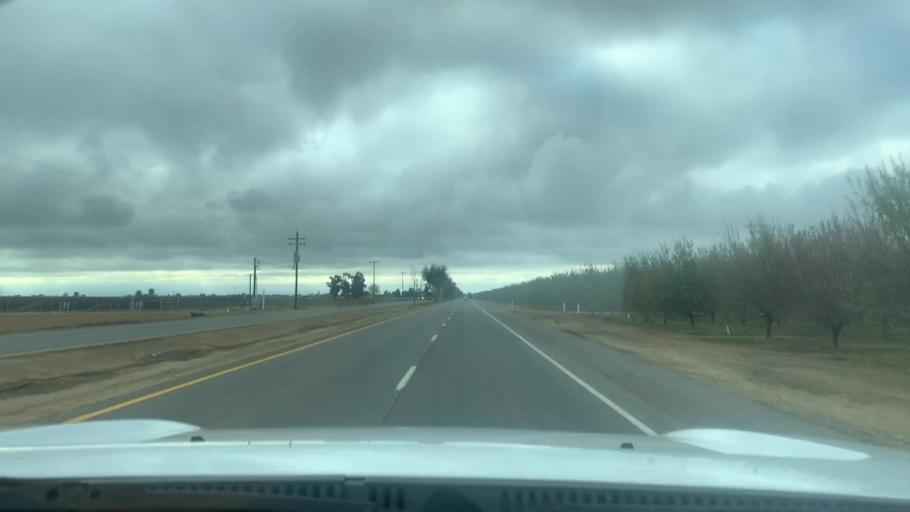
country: US
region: California
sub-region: Kern County
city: Shafter
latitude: 35.4998
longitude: -119.2329
